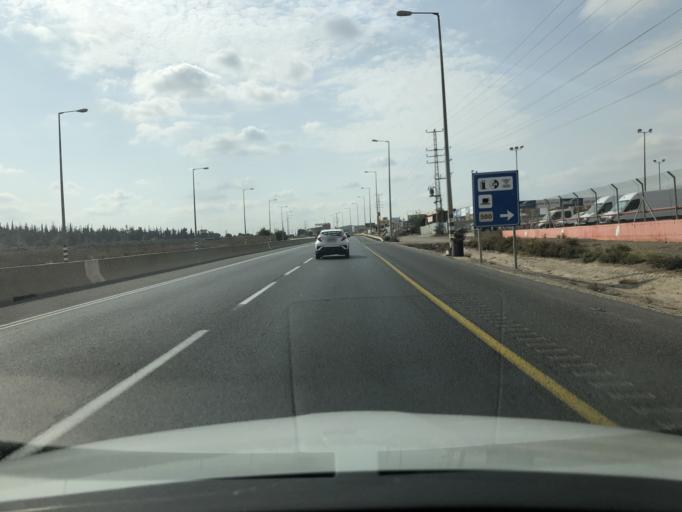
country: IL
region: Central District
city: Tirah
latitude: 32.2281
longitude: 34.9824
